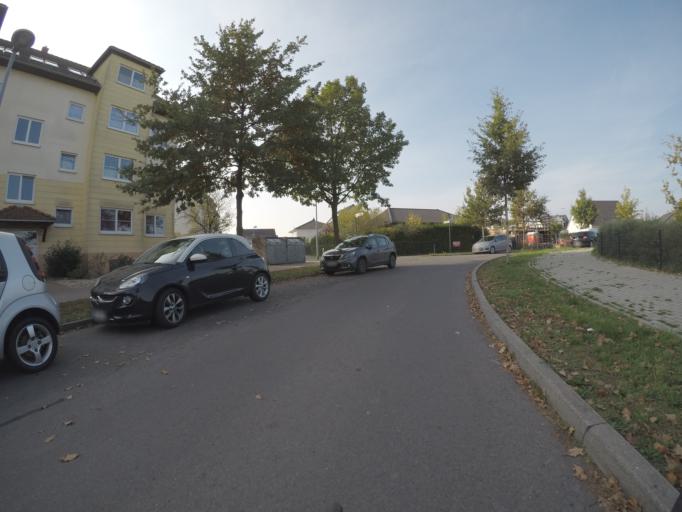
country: DE
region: Berlin
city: Gropiusstadt
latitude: 52.4014
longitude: 13.4536
